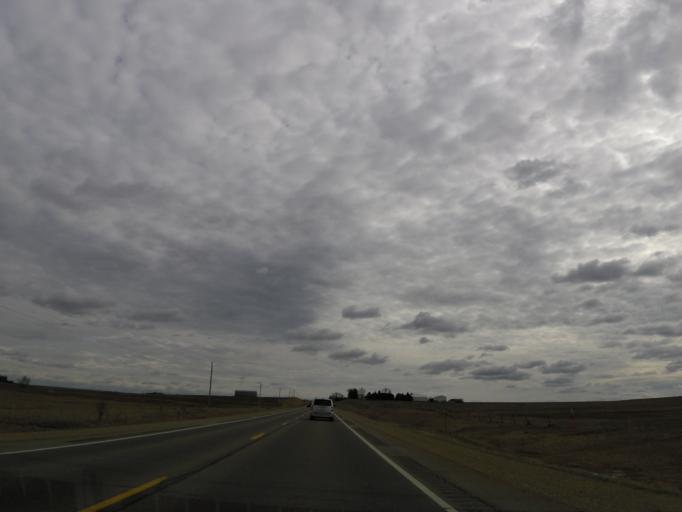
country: US
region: Iowa
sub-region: Chickasaw County
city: New Hampton
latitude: 43.1679
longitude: -92.2989
